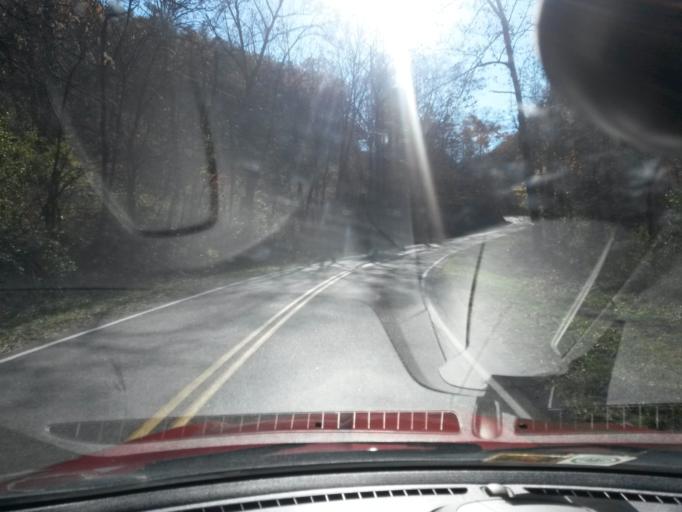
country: US
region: Virginia
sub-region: Botetourt County
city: Buchanan
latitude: 37.5222
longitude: -79.6668
